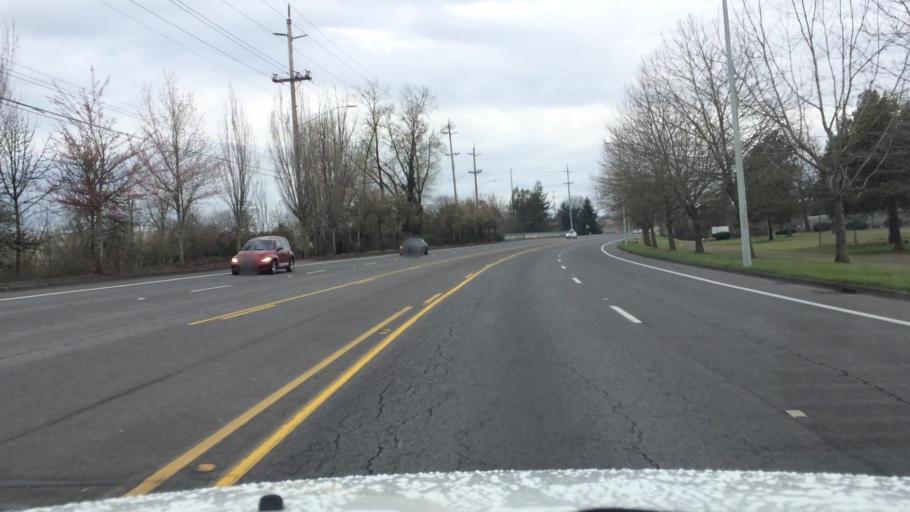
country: US
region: Oregon
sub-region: Marion County
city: Four Corners
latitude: 44.9281
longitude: -122.9996
